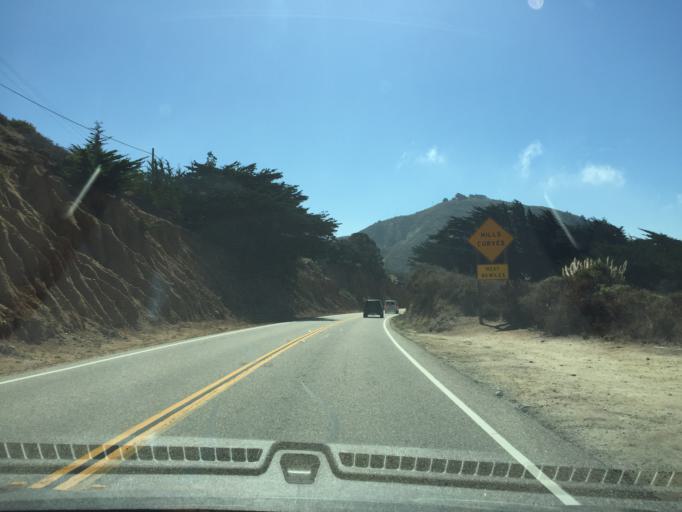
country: US
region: California
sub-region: Monterey County
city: Carmel-by-the-Sea
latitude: 36.3841
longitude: -121.9002
